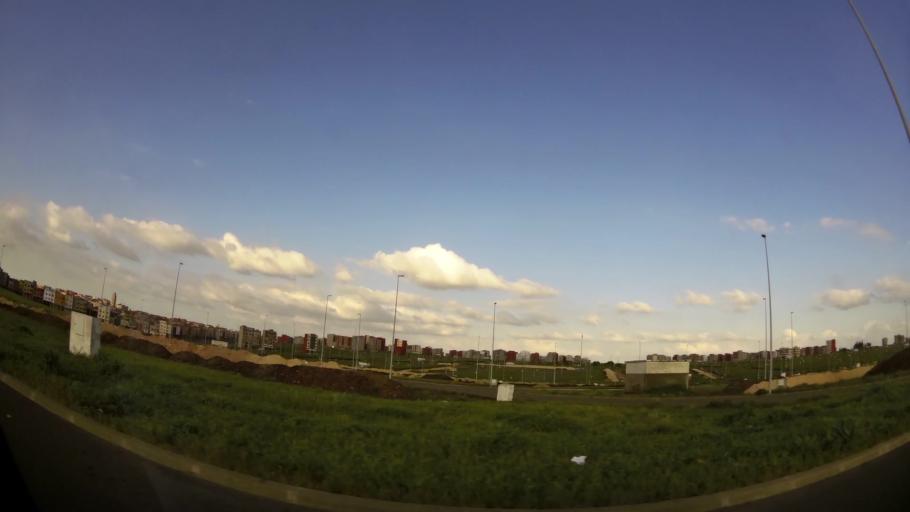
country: MA
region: Chaouia-Ouardigha
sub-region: Settat Province
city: Settat
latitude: 32.9902
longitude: -7.6445
